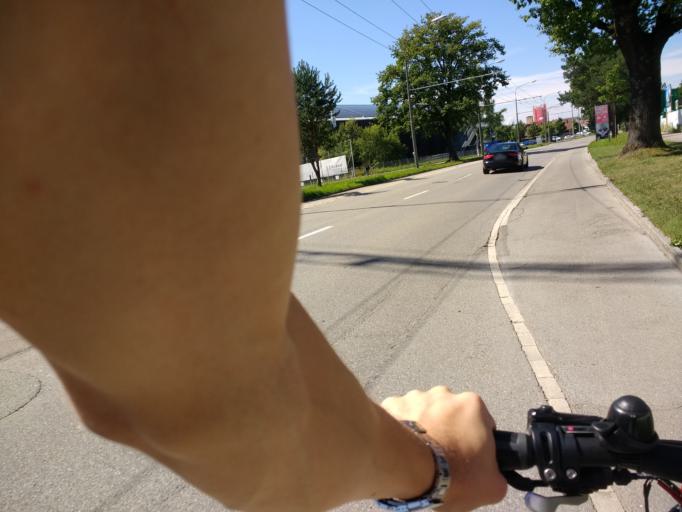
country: CH
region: Zurich
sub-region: Bezirk Winterthur
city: Mattenbach (Kreis 7) / Gutschick
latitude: 47.4951
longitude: 8.7499
